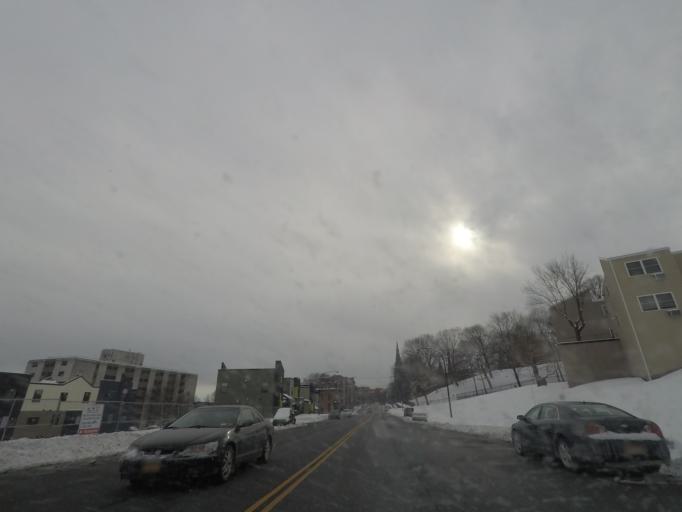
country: US
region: New York
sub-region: Albany County
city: Albany
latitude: 42.6600
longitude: -73.7501
